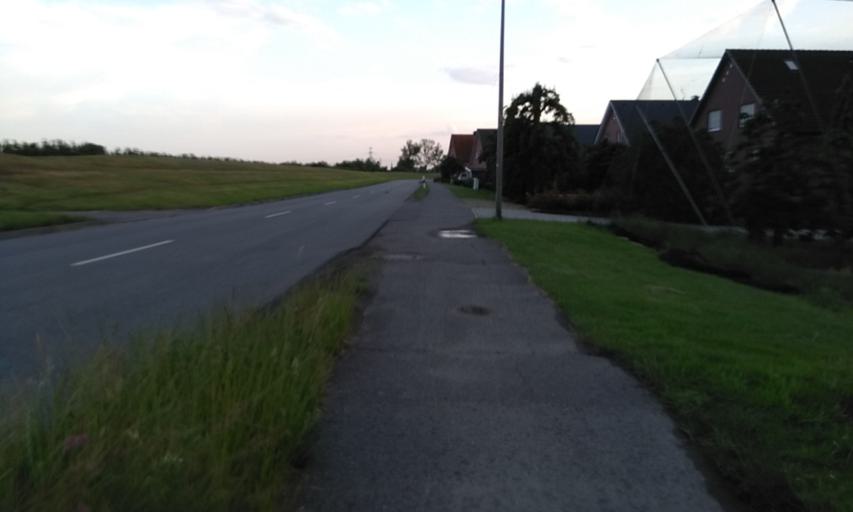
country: DE
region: Lower Saxony
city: Buxtehude
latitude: 53.5008
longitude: 9.7249
